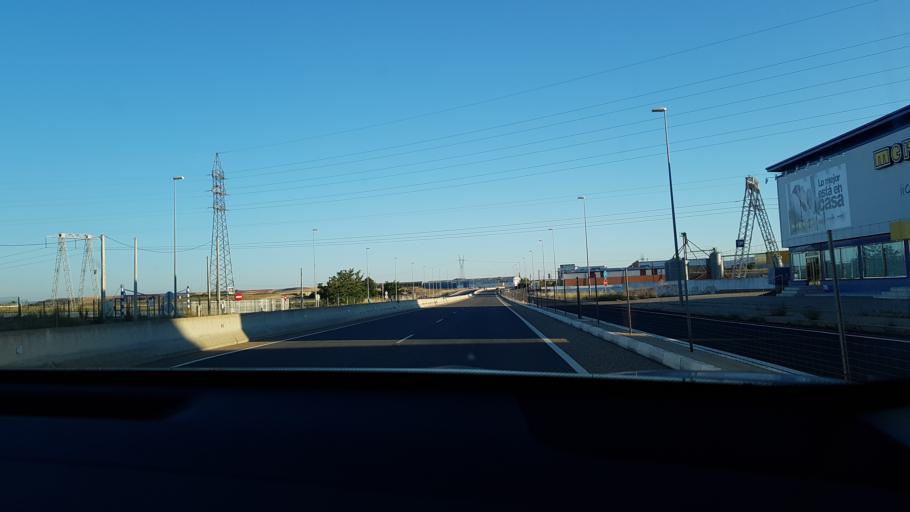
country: ES
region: Castille and Leon
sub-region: Provincia de Zamora
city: Valcabado
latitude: 41.5342
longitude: -5.7613
